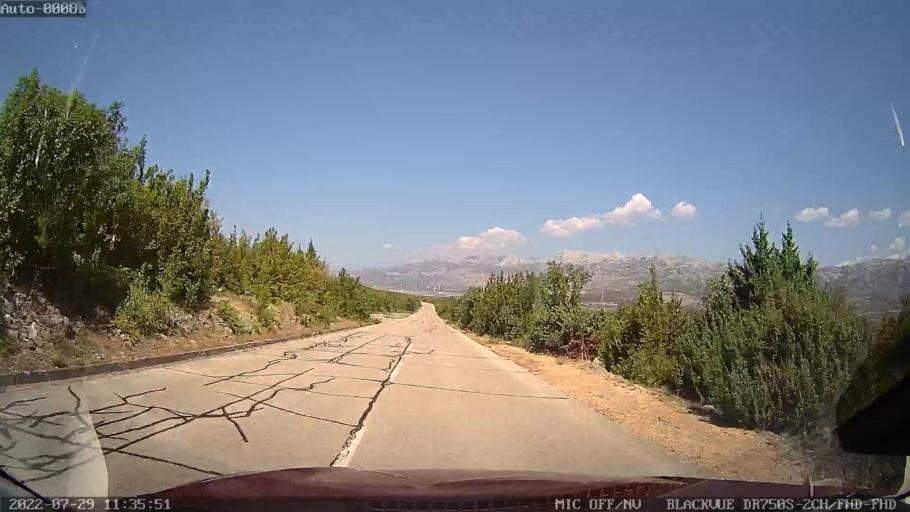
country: HR
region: Zadarska
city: Obrovac
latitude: 44.1847
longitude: 15.7058
